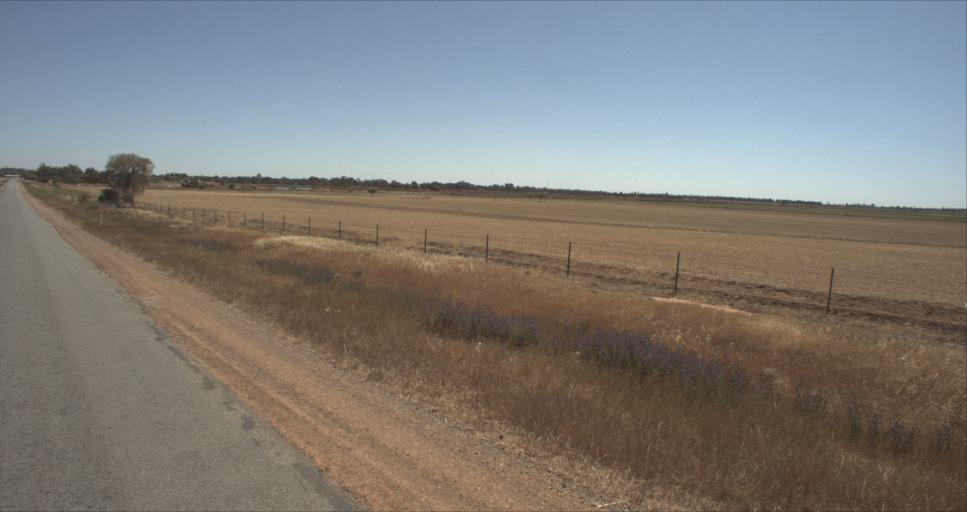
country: AU
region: New South Wales
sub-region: Leeton
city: Leeton
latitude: -34.5413
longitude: 146.4363
